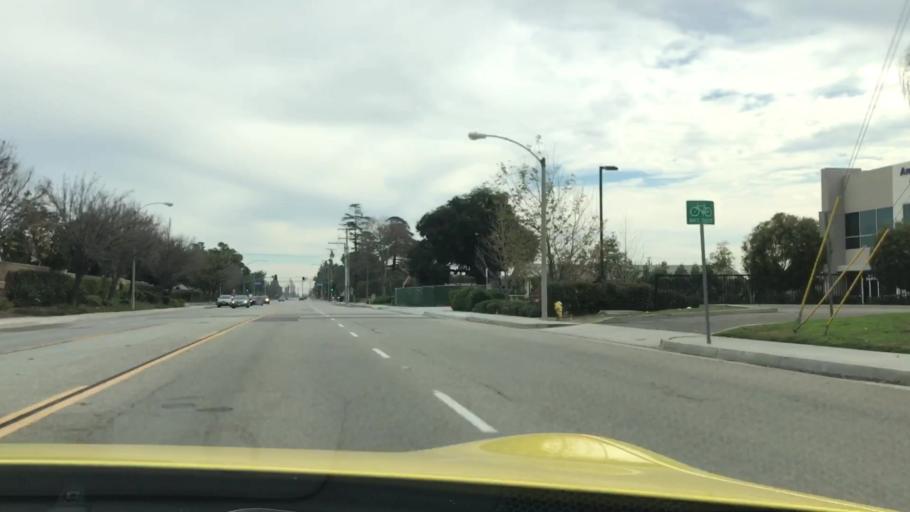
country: US
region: California
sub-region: San Bernardino County
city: Chino
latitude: 34.0117
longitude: -117.7048
